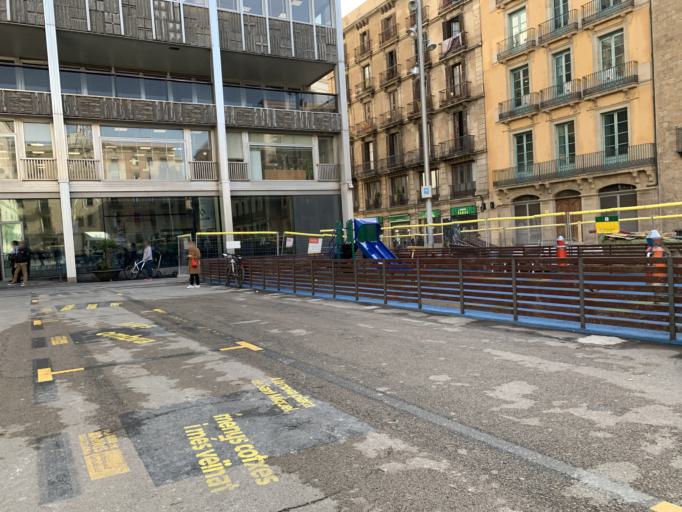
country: ES
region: Catalonia
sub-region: Provincia de Barcelona
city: Ciutat Vella
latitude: 41.3820
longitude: 2.1773
